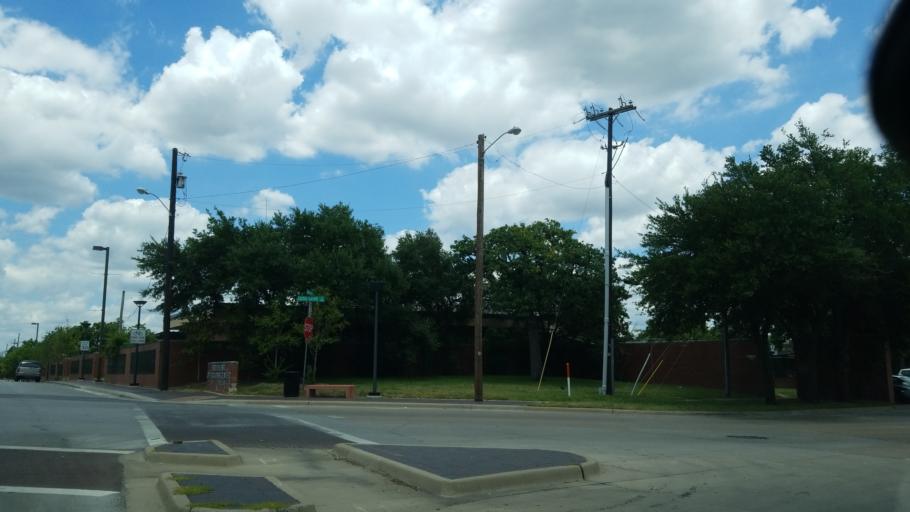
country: US
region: Texas
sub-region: Dallas County
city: Dallas
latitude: 32.7382
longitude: -96.7534
